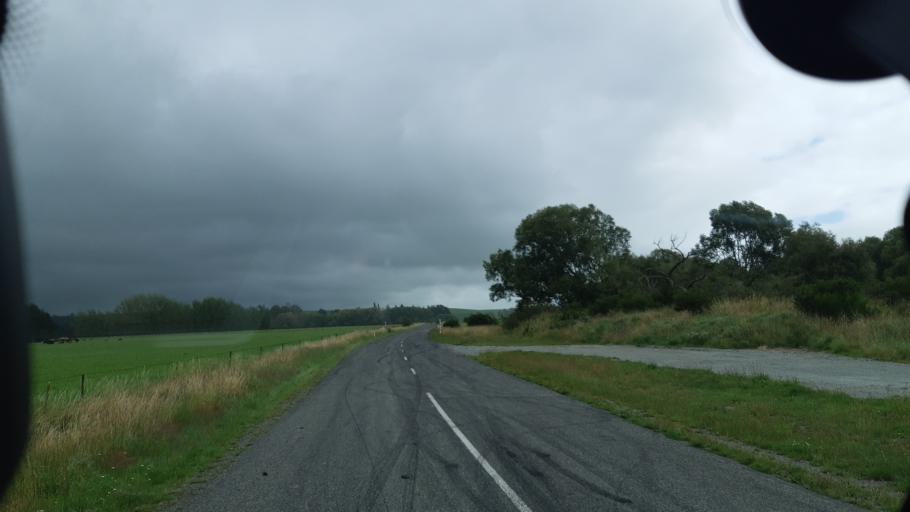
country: NZ
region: Canterbury
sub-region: Timaru District
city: Pleasant Point
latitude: -44.3969
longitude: 170.9973
